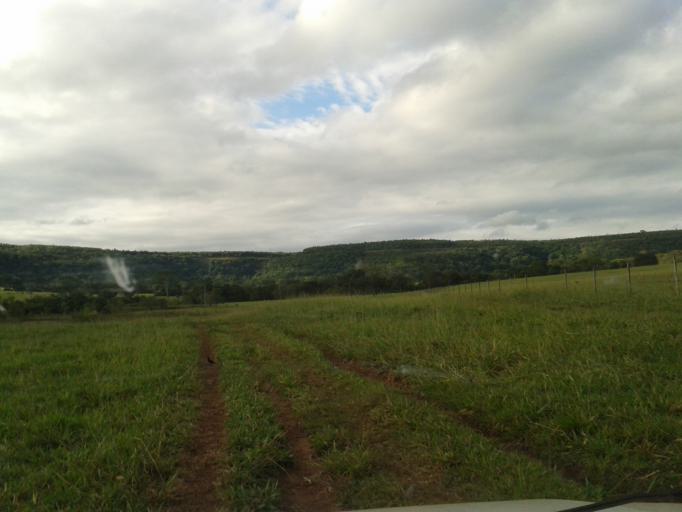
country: BR
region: Minas Gerais
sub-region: Campina Verde
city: Campina Verde
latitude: -19.4657
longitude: -49.6320
